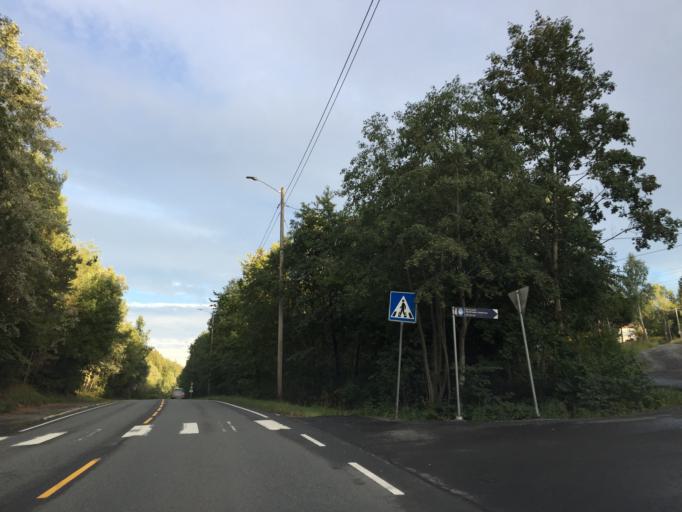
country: NO
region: Akershus
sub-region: Oppegard
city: Kolbotn
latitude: 59.8404
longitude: 10.8283
